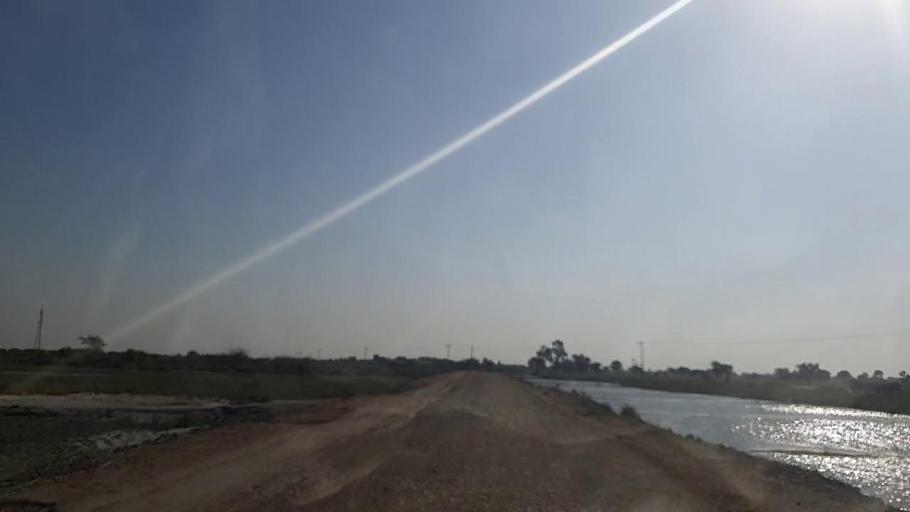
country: PK
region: Sindh
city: Mirpur Batoro
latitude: 24.5995
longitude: 68.1703
